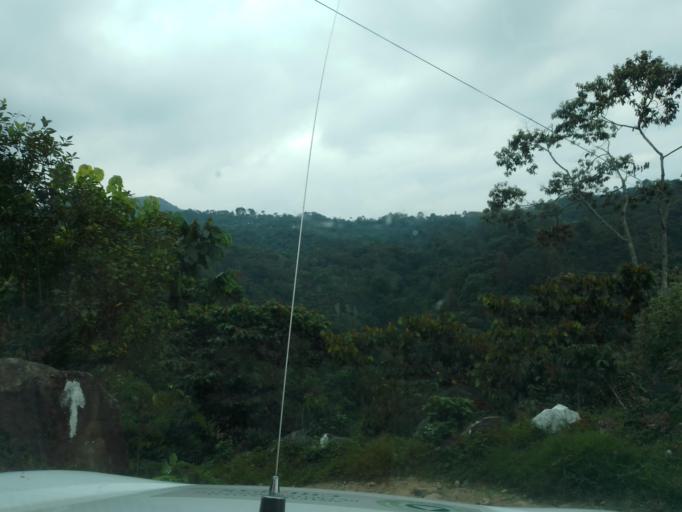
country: MX
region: Chiapas
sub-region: Union Juarez
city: Santo Domingo
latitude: 15.0696
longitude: -92.1242
